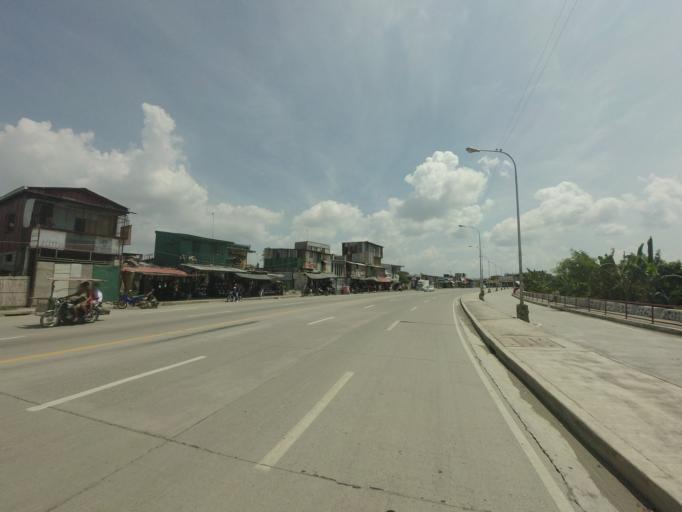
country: PH
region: Calabarzon
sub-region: Province of Rizal
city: Taguig
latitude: 14.5333
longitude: 121.1067
